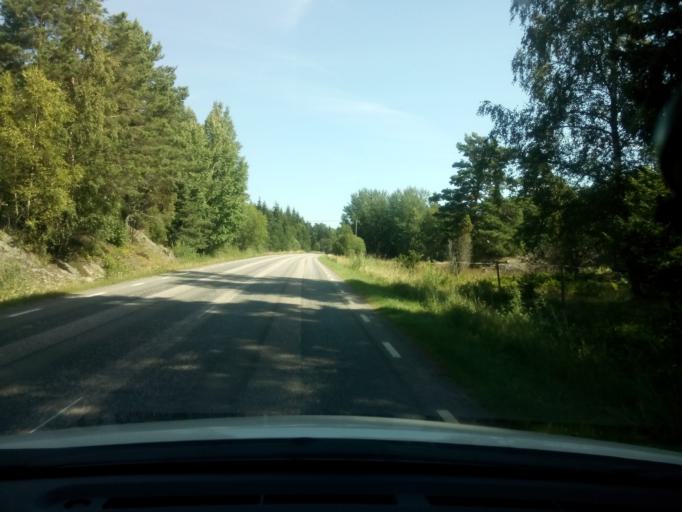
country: SE
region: Soedermanland
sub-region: Oxelosunds Kommun
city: Oxelosund
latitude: 58.7472
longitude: 17.2666
